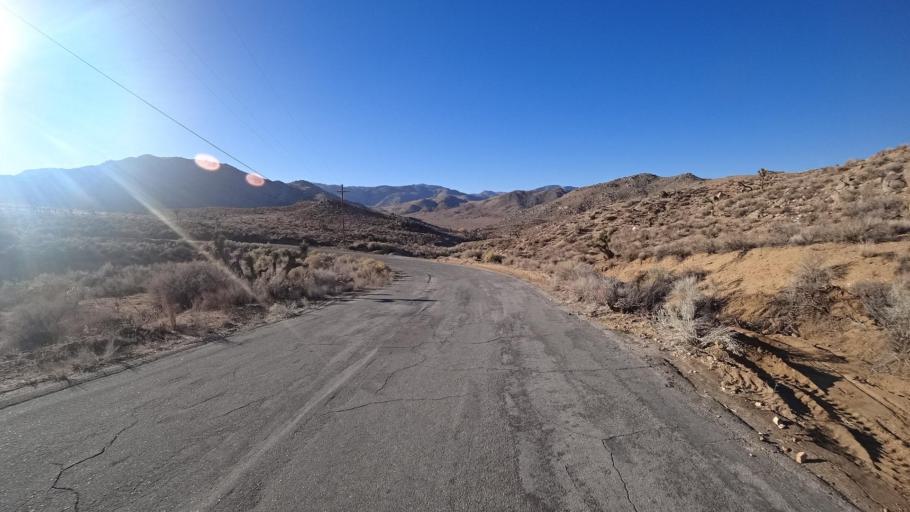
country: US
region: California
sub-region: Kern County
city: Weldon
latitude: 35.5244
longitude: -118.2018
